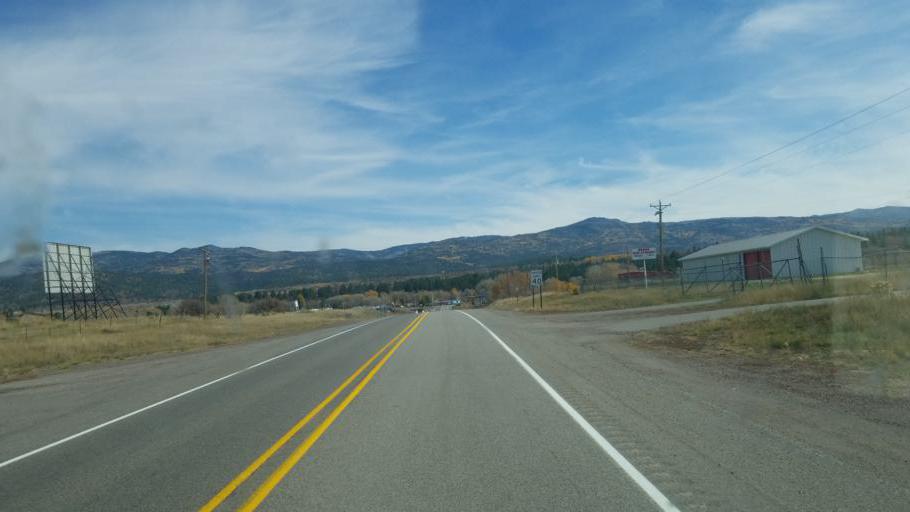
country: US
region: New Mexico
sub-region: Rio Arriba County
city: Chama
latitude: 36.8831
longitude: -106.5921
